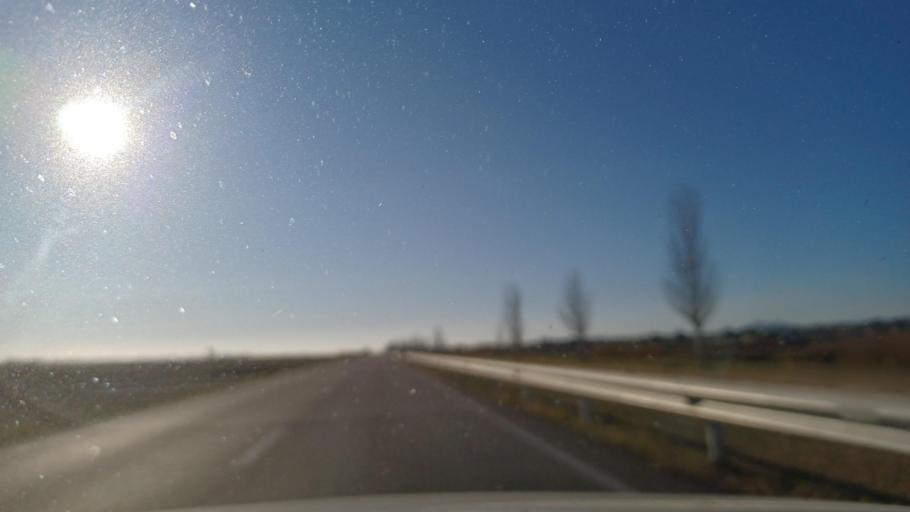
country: ES
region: Catalonia
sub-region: Provincia de Tarragona
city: Sant Carles de la Rapita
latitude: 40.6569
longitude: 0.5937
